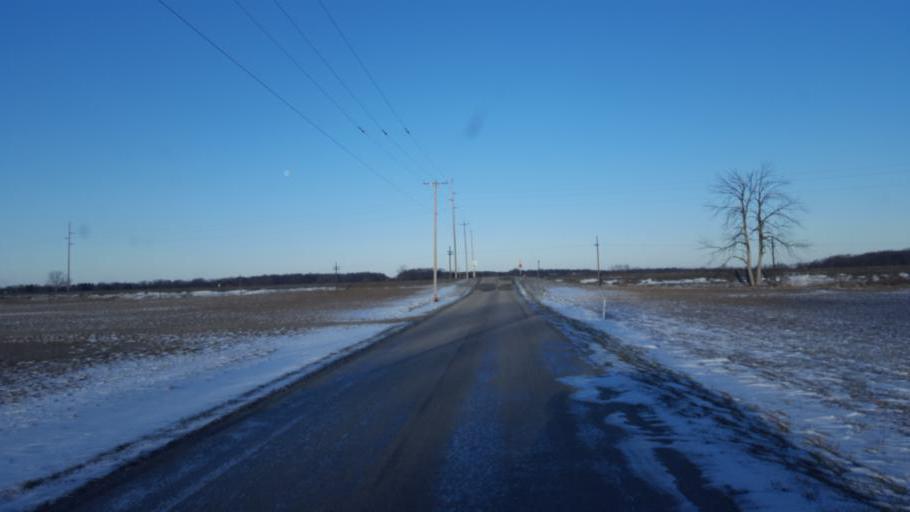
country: US
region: Ohio
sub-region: Morrow County
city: Cardington
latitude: 40.5164
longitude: -82.8856
